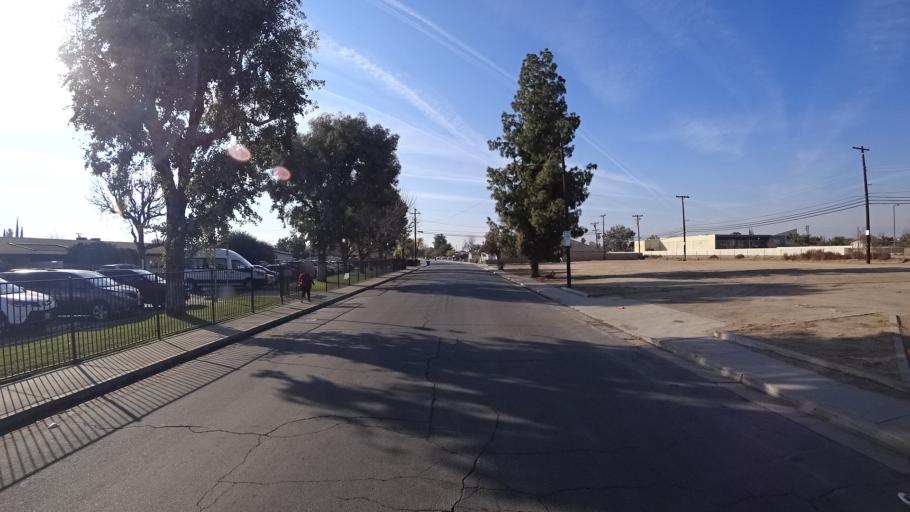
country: US
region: California
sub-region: Kern County
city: Bakersfield
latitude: 35.3235
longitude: -119.0220
